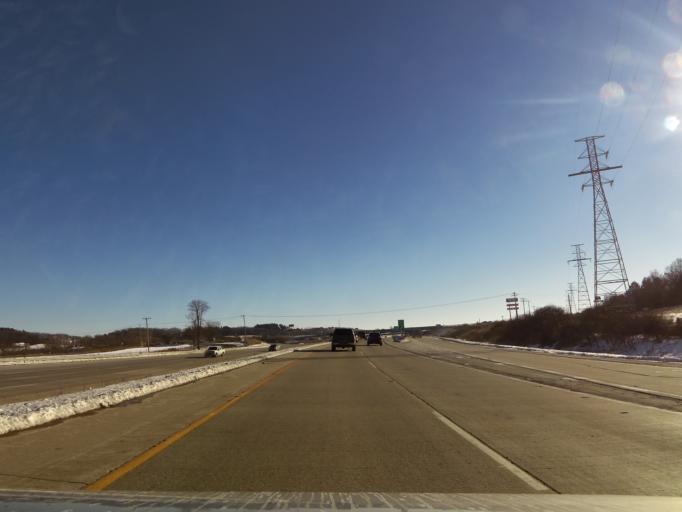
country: US
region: Wisconsin
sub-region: Columbia County
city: Portage
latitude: 43.4945
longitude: -89.4962
